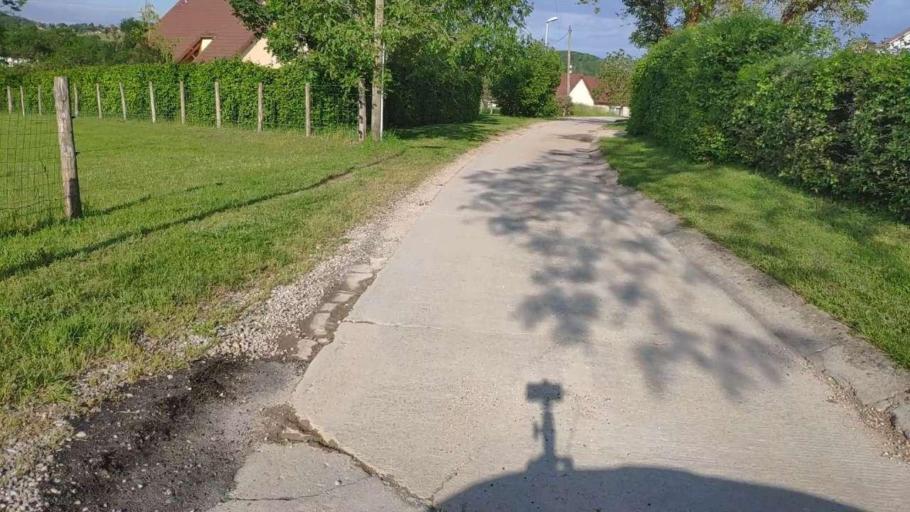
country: FR
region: Franche-Comte
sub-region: Departement du Jura
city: Perrigny
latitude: 46.7286
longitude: 5.5950
